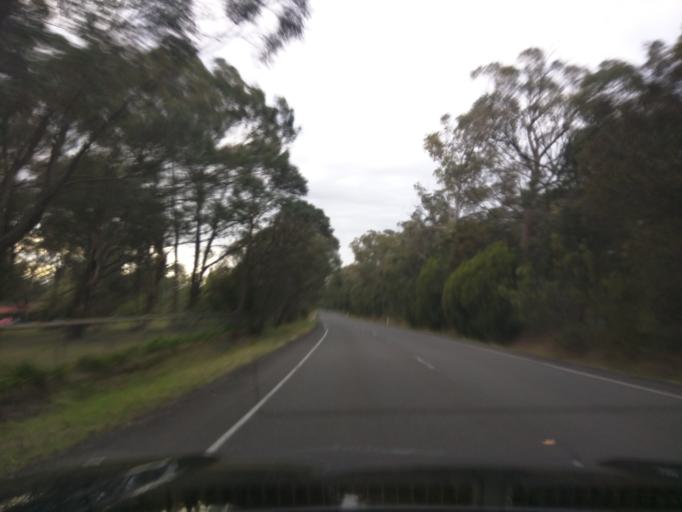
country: AU
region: New South Wales
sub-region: Wollondilly
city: Douglas Park
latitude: -34.2447
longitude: 150.7272
